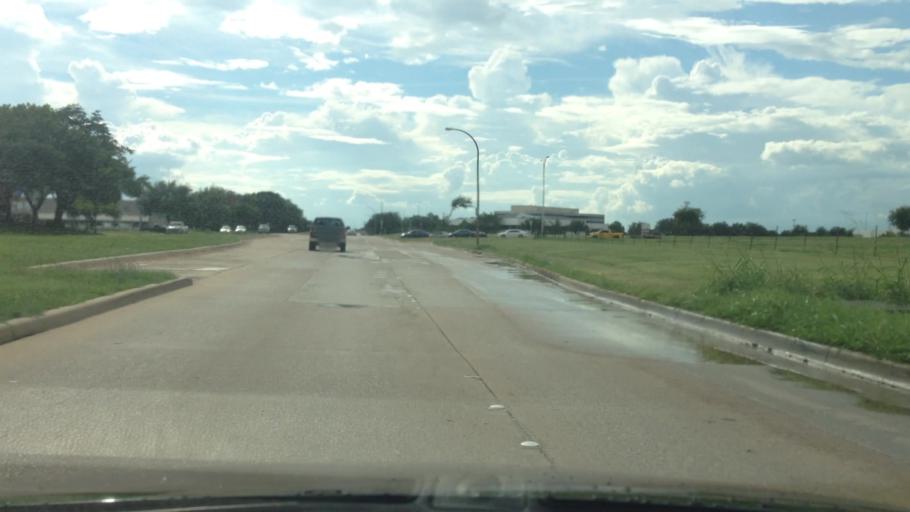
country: US
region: Texas
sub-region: Tarrant County
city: Haltom City
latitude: 32.8244
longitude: -97.2983
